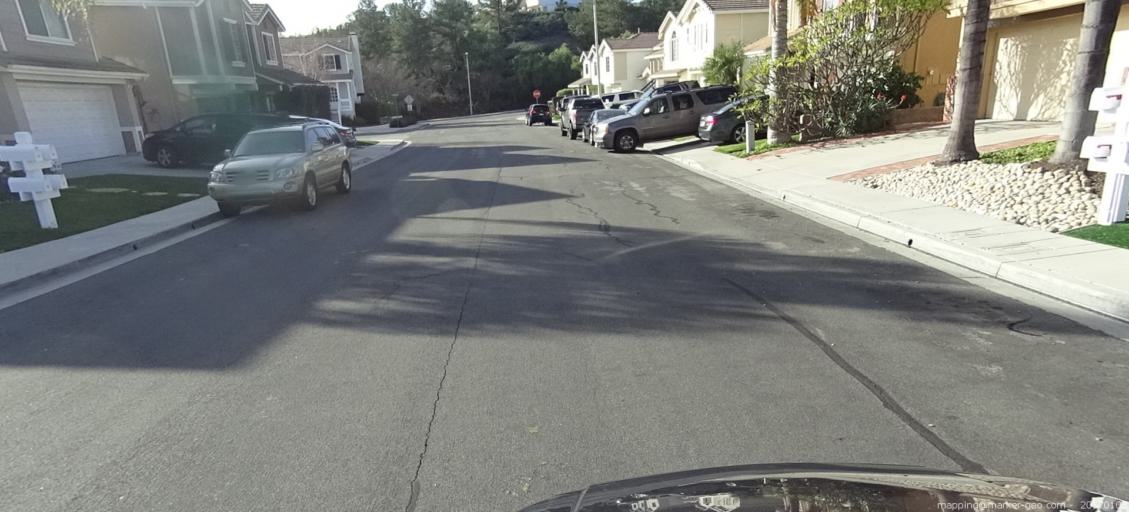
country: US
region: California
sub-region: Orange County
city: Coto De Caza
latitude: 33.5926
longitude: -117.5956
